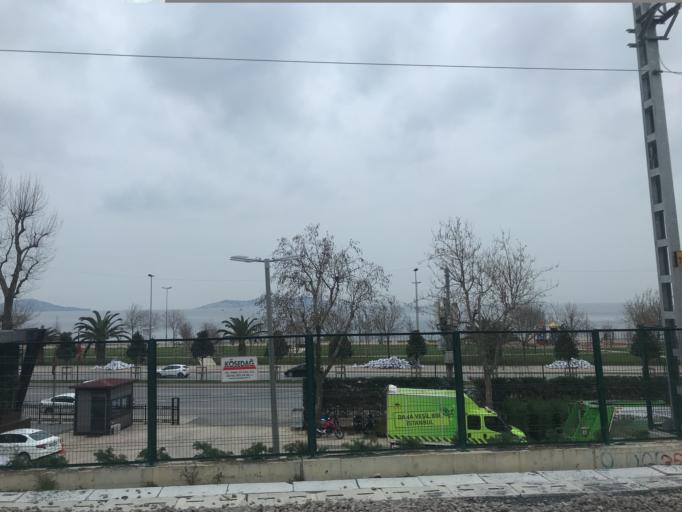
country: TR
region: Istanbul
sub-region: Atasehir
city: Atasehir
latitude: 40.9482
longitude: 29.1019
